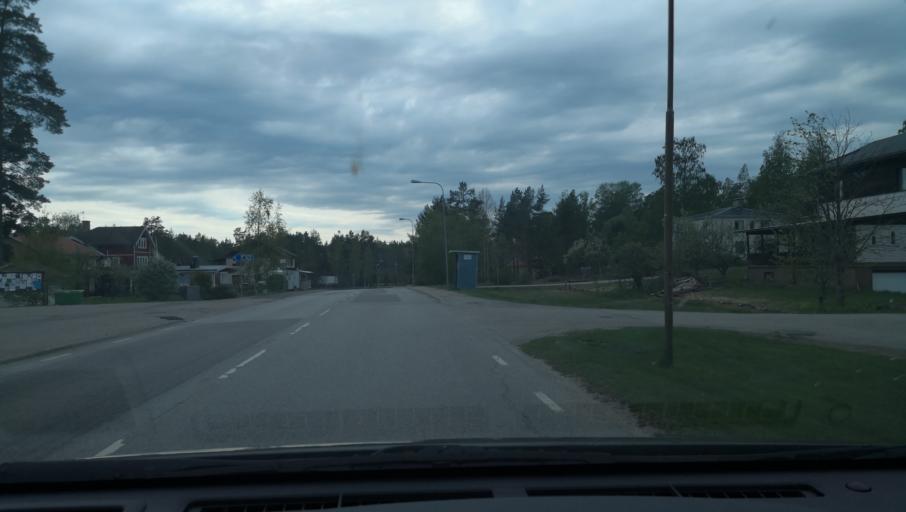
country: SE
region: Vaestmanland
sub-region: Skinnskattebergs Kommun
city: Skinnskatteberg
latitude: 59.8082
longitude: 15.5476
